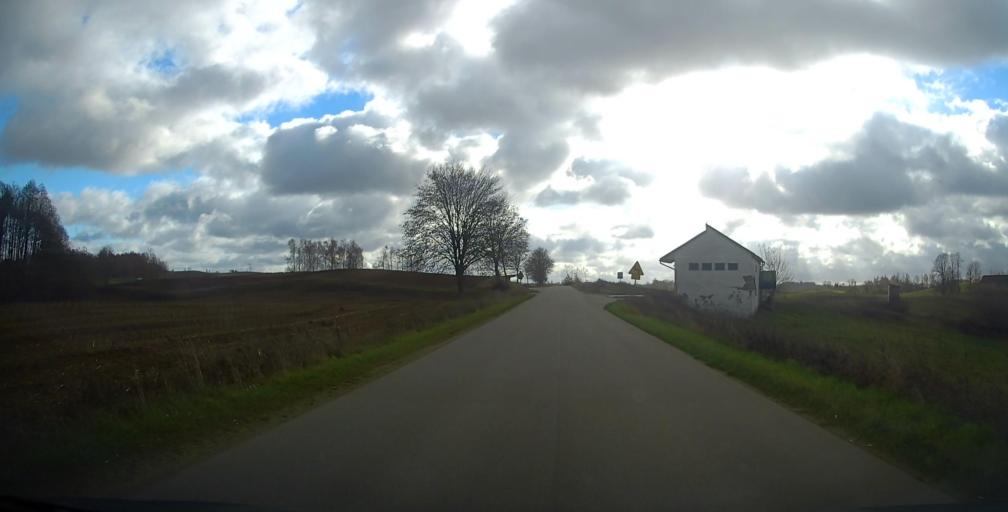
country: PL
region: Podlasie
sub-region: Suwalki
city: Suwalki
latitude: 54.3312
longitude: 22.8594
